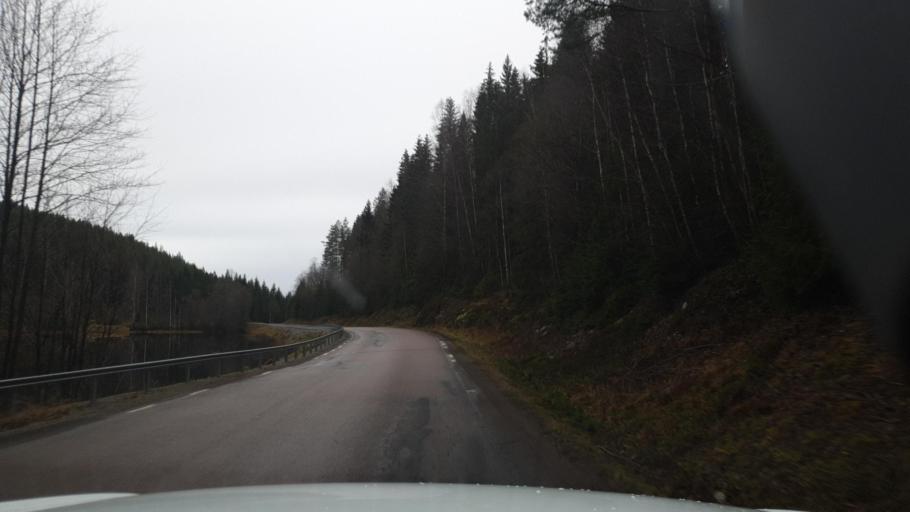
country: SE
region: Vaermland
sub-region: Arvika Kommun
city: Arvika
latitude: 59.7011
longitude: 12.7911
